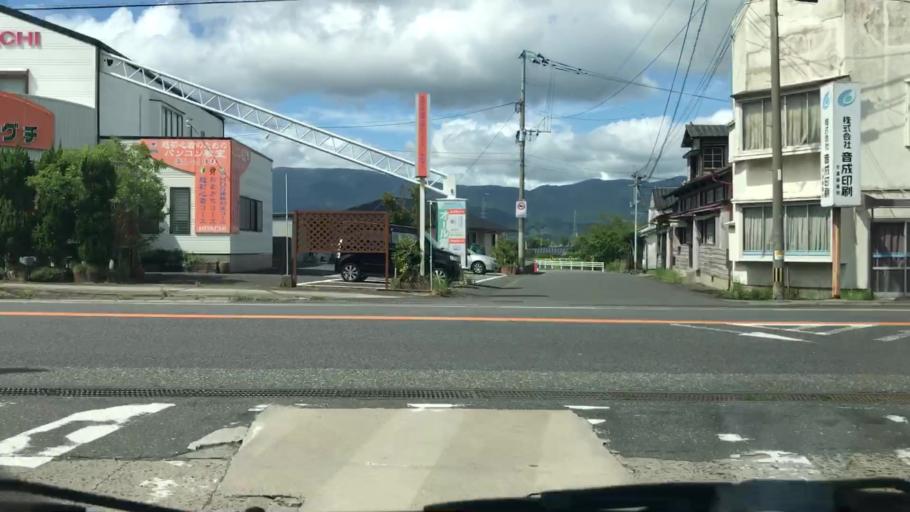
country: JP
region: Saga Prefecture
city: Saga-shi
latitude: 33.2493
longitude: 130.2009
